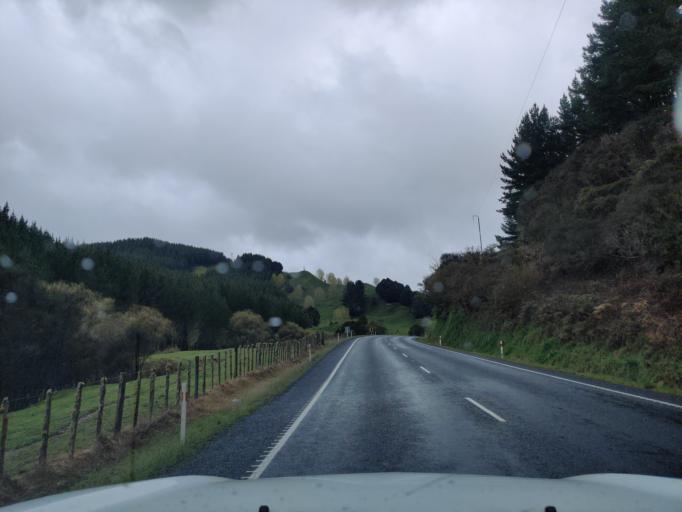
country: NZ
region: Waikato
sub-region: Otorohanga District
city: Otorohanga
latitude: -38.6629
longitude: 175.2066
